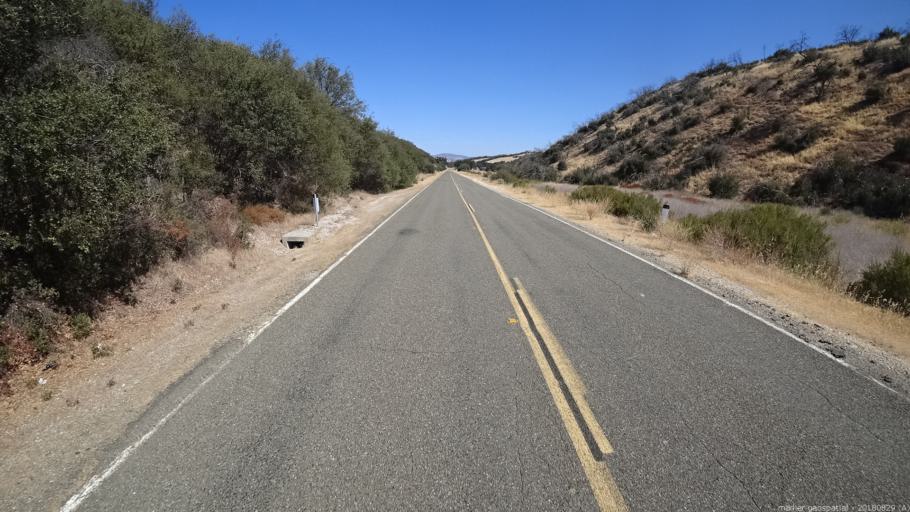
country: US
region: California
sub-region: San Luis Obispo County
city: Lake Nacimiento
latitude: 35.8652
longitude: -121.0623
